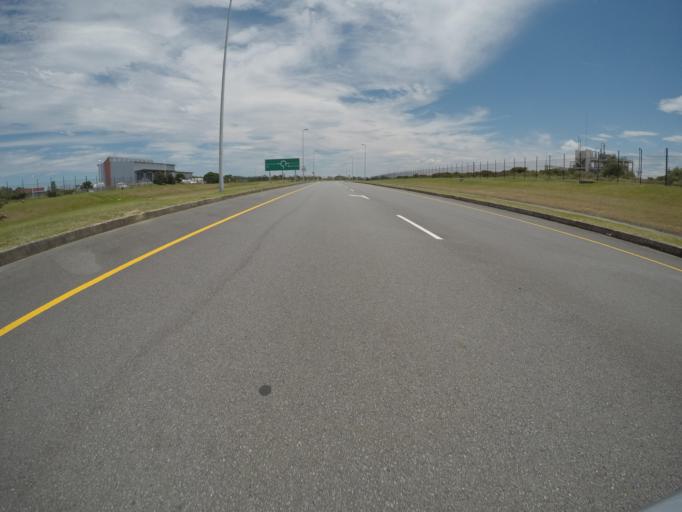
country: ZA
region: Eastern Cape
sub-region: Buffalo City Metropolitan Municipality
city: East London
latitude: -33.0565
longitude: 27.8366
